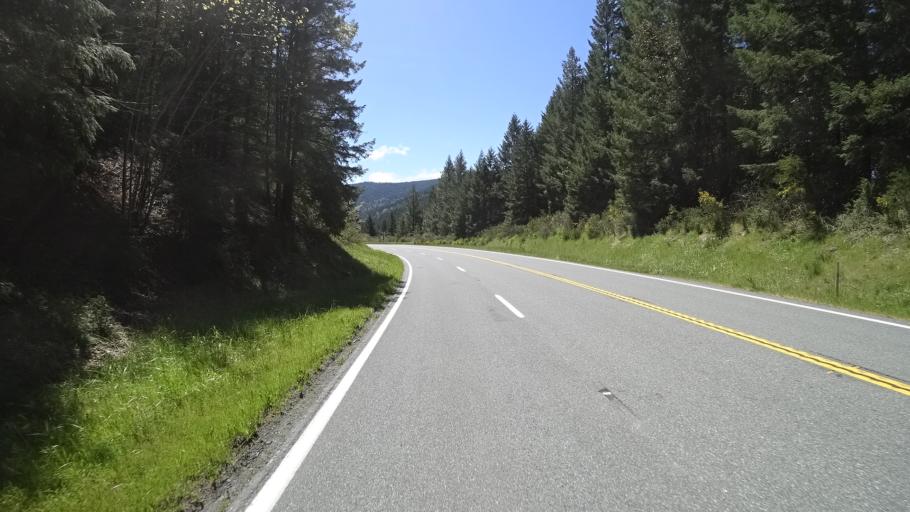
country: US
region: California
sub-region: Humboldt County
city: Blue Lake
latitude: 40.9108
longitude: -123.8097
